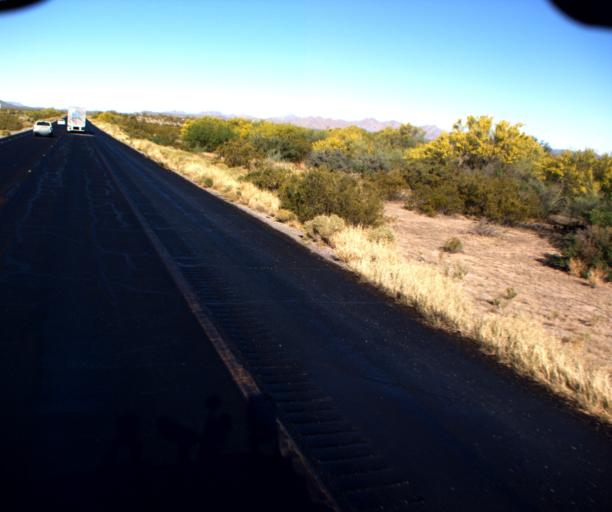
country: US
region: Arizona
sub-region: Pinal County
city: Maricopa
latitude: 32.8365
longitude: -112.2037
